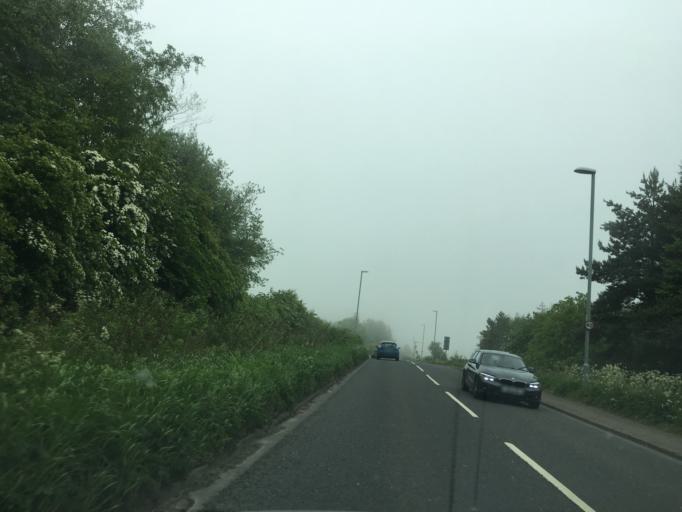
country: GB
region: Scotland
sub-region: Midlothian
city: Penicuik
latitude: 55.8502
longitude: -3.1910
